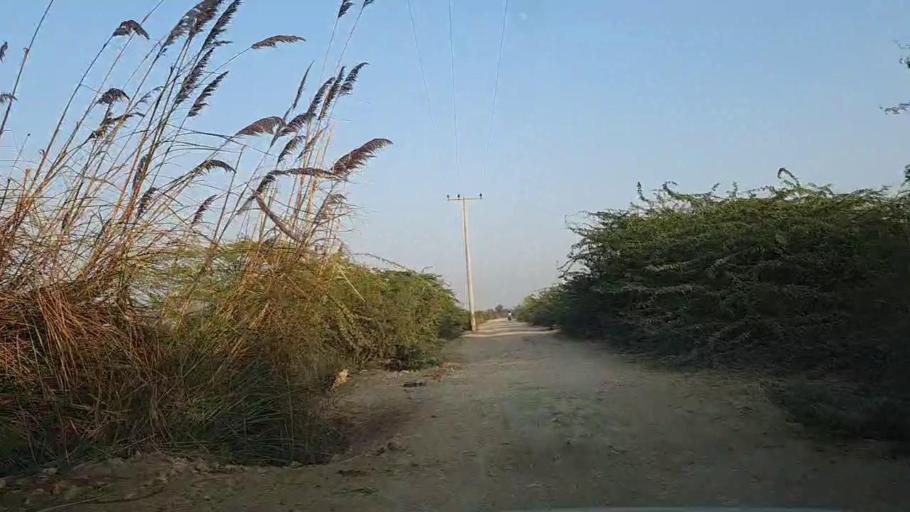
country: PK
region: Sindh
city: Keti Bandar
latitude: 24.2767
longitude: 67.6597
